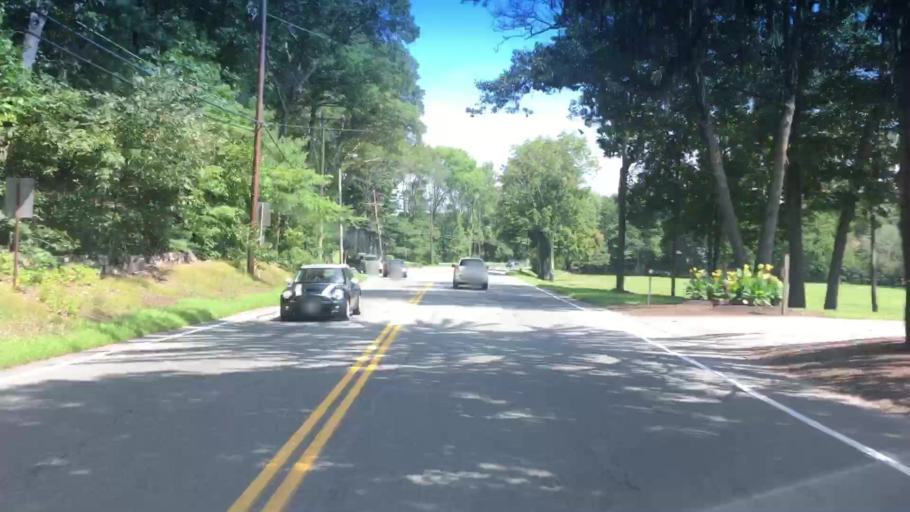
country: US
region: Massachusetts
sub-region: Norfolk County
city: Medfield
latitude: 42.1946
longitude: -71.2895
